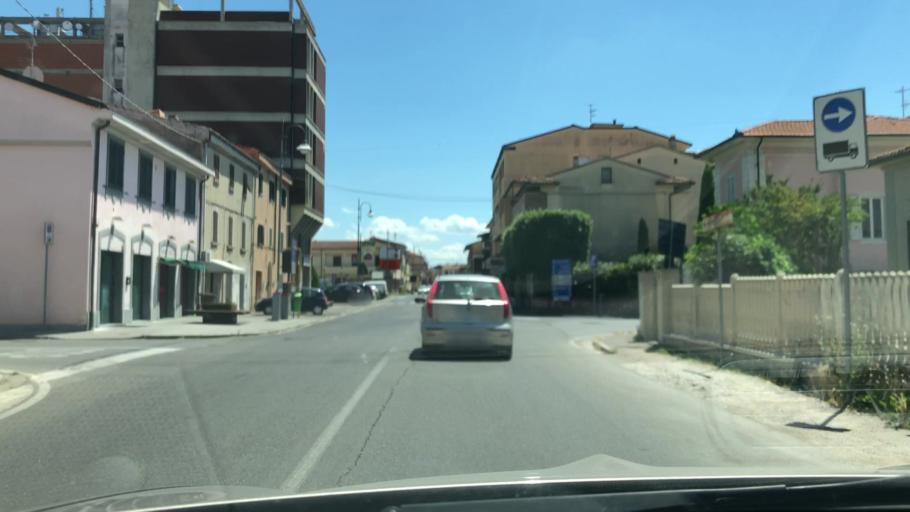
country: IT
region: Tuscany
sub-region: Province of Pisa
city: Ponsacco
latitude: 43.6246
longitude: 10.6297
